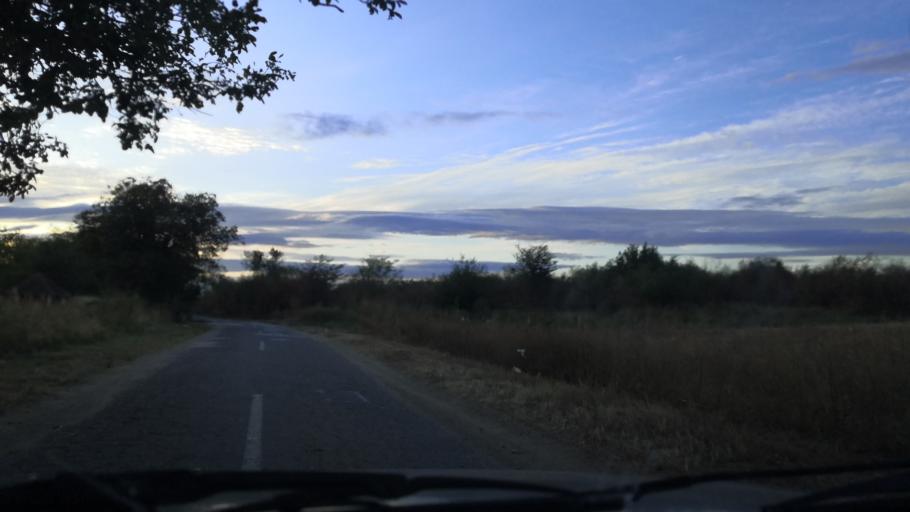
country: RO
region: Mehedinti
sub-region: Comuna Gruia
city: Izvoarele
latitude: 44.2743
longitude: 22.6629
